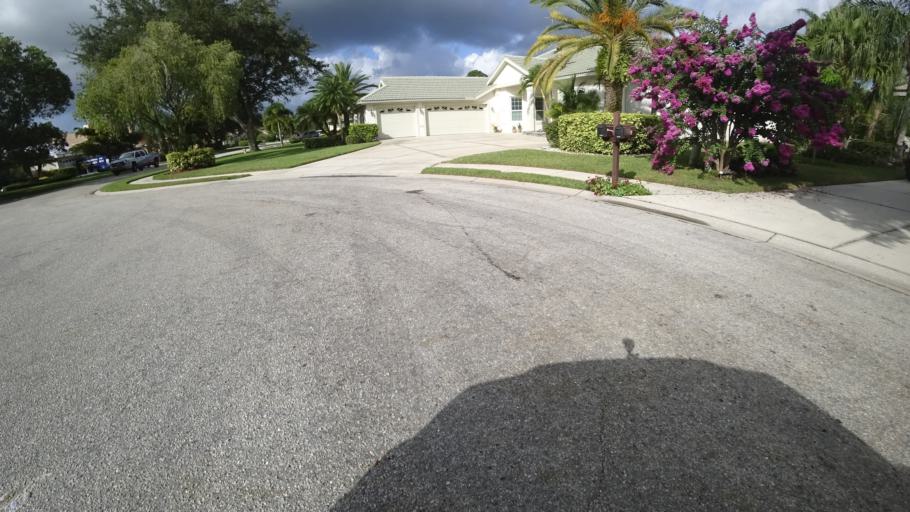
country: US
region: Florida
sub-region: Sarasota County
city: Desoto Lakes
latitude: 27.4134
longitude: -82.4831
